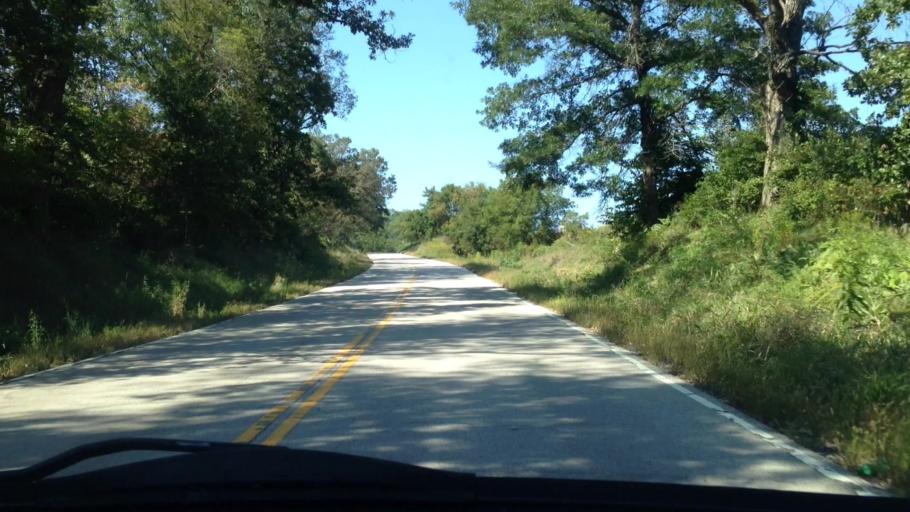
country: US
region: Minnesota
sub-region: Fillmore County
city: Rushford
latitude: 43.6648
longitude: -91.7931
